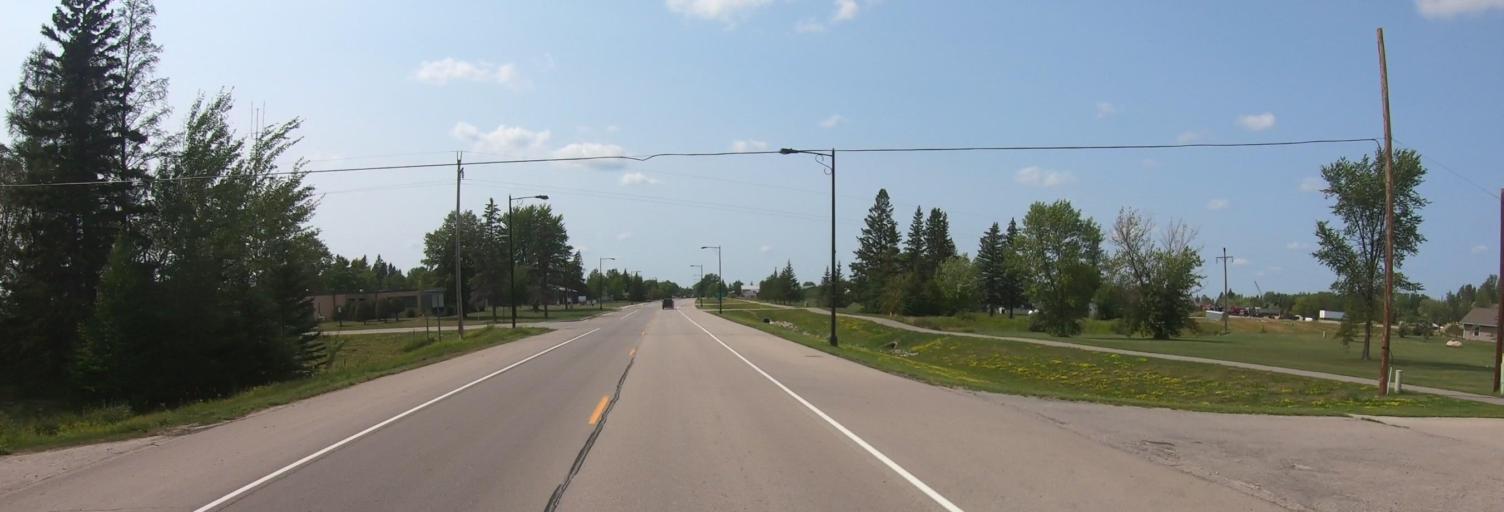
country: US
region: Minnesota
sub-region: Lake of the Woods County
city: Baudette
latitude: 48.7116
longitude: -94.5823
